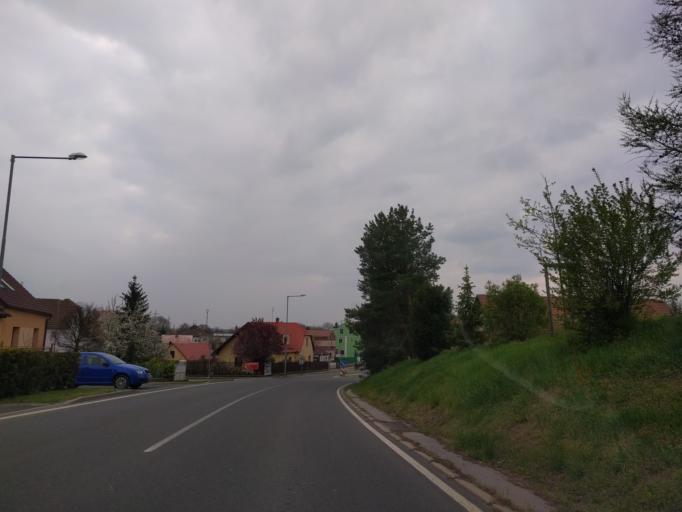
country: CZ
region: Central Bohemia
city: Cesky Brod
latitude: 50.0795
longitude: 14.8649
